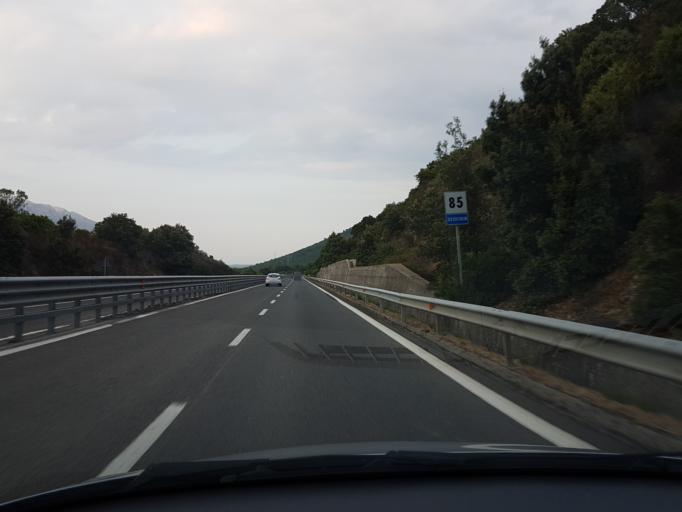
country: IT
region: Sardinia
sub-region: Provincia di Nuoro
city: Loculi
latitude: 40.4902
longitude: 9.6066
